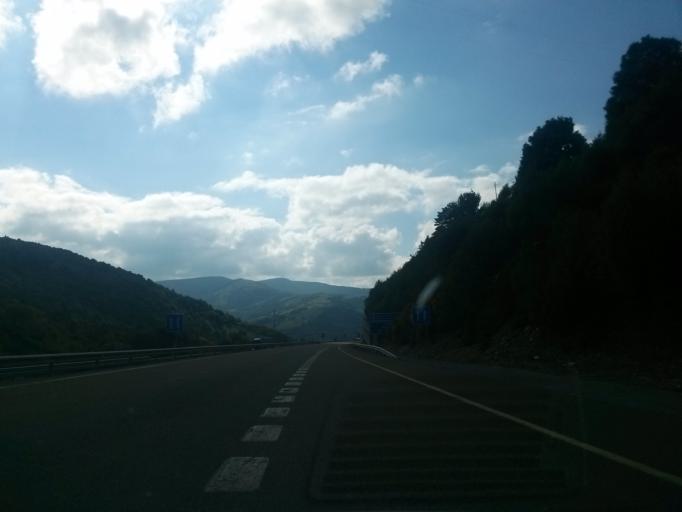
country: ES
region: Castille and Leon
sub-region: Provincia de Leon
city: Balboa
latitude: 42.7273
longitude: -7.0348
